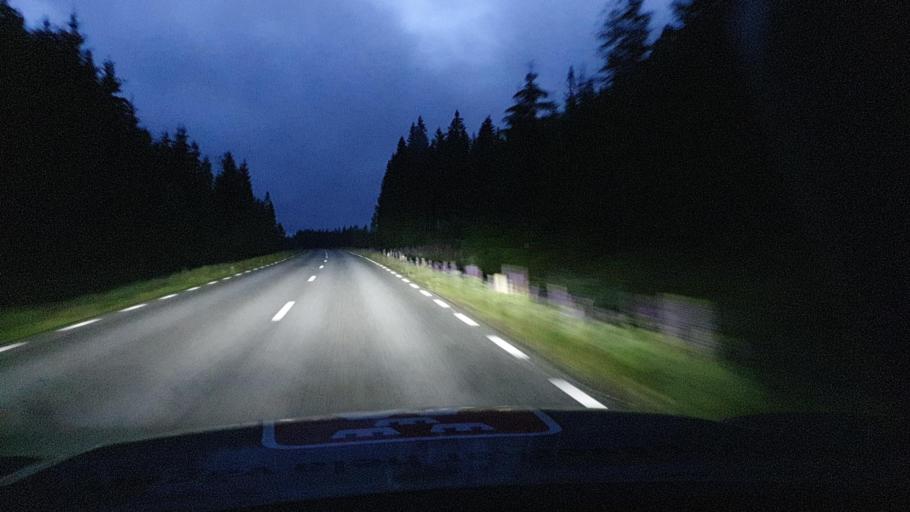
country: SE
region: OErebro
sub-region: Karlskoga Kommun
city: Karlskoga
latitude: 59.5103
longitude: 14.4938
